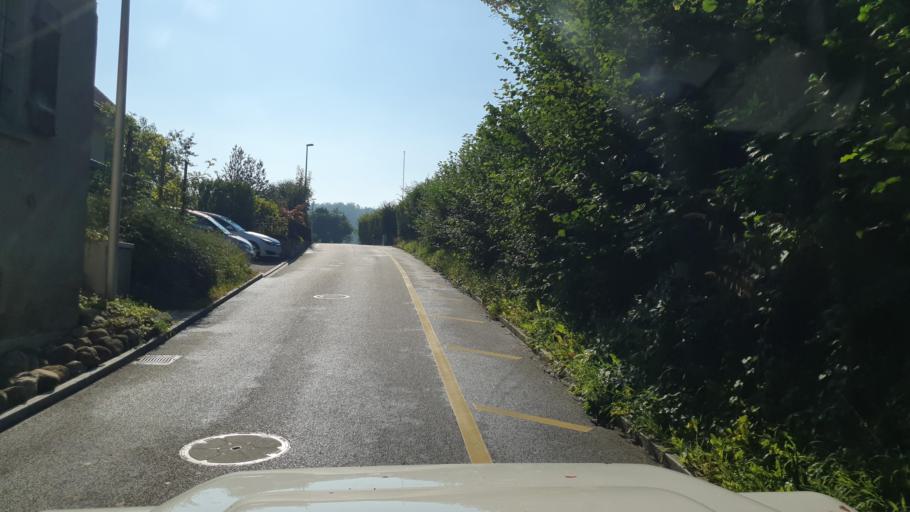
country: CH
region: Aargau
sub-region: Bezirk Bremgarten
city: Villmergen
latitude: 47.3417
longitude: 8.2477
